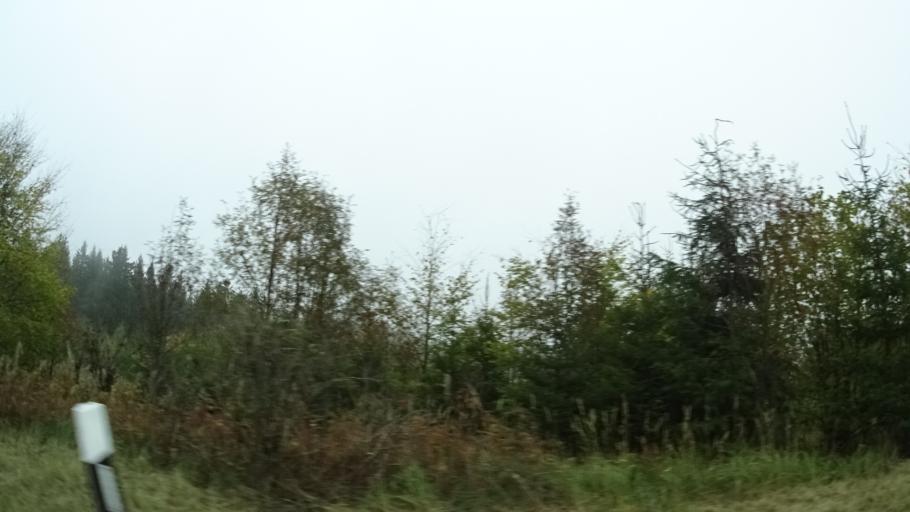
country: DE
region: Thuringia
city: Birx
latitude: 50.5504
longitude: 10.0486
